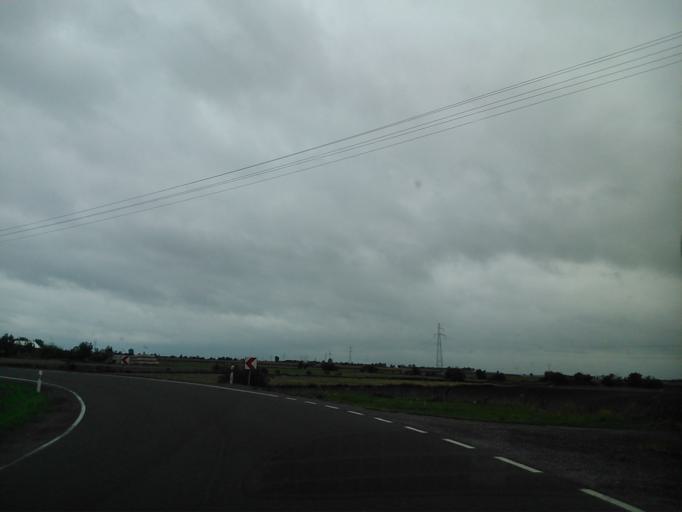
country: PL
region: Kujawsko-Pomorskie
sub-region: Powiat mogilenski
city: Strzelno
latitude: 52.6671
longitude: 18.2351
